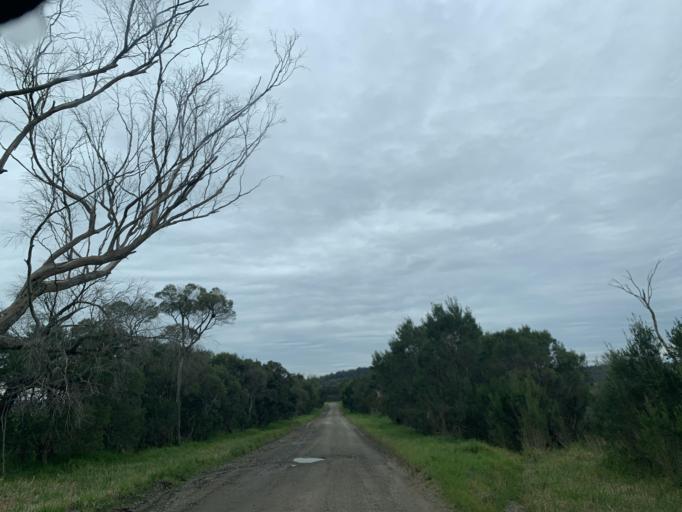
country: AU
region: Victoria
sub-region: Cardinia
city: Garfield
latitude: -38.0944
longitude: 145.6415
